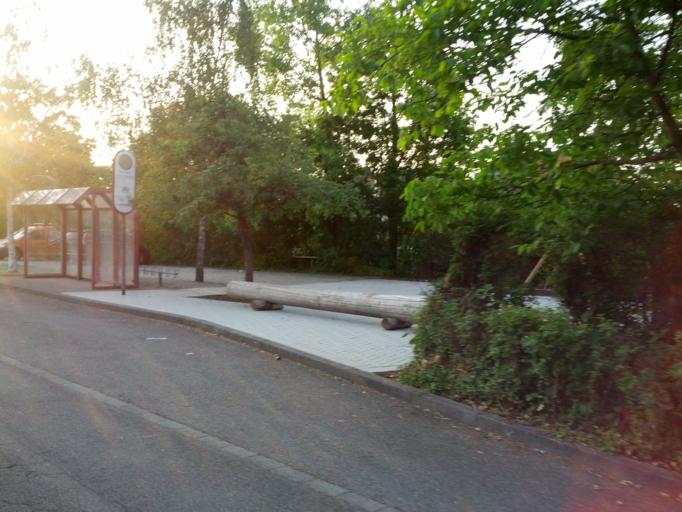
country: DE
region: Baden-Wuerttemberg
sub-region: Freiburg Region
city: Herbolzheim
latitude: 48.2223
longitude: 7.7695
